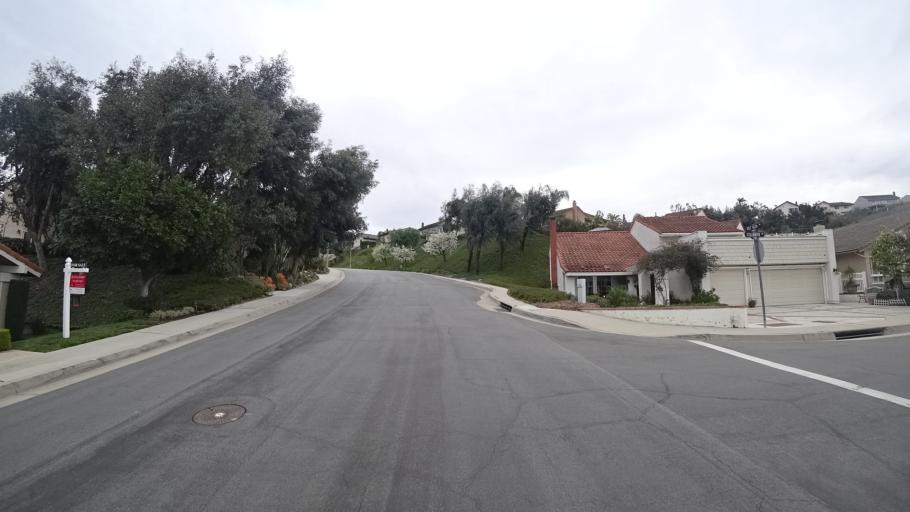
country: US
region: California
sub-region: Orange County
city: Villa Park
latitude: 33.8378
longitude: -117.7652
